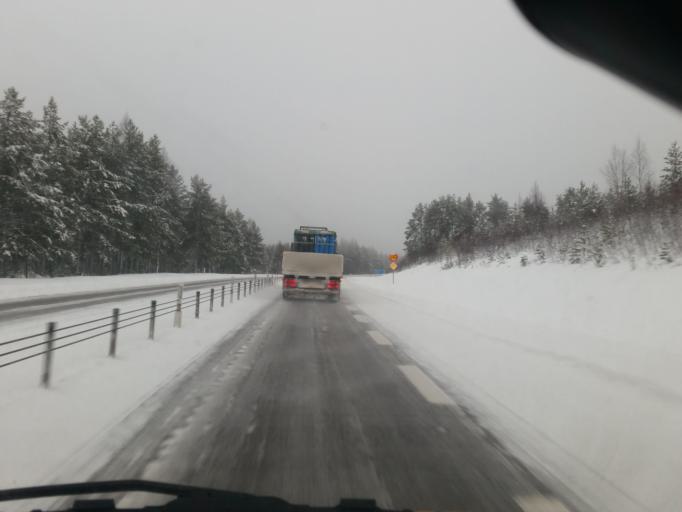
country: SE
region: Norrbotten
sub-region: Pitea Kommun
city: Pitea
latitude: 65.1630
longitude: 21.4928
